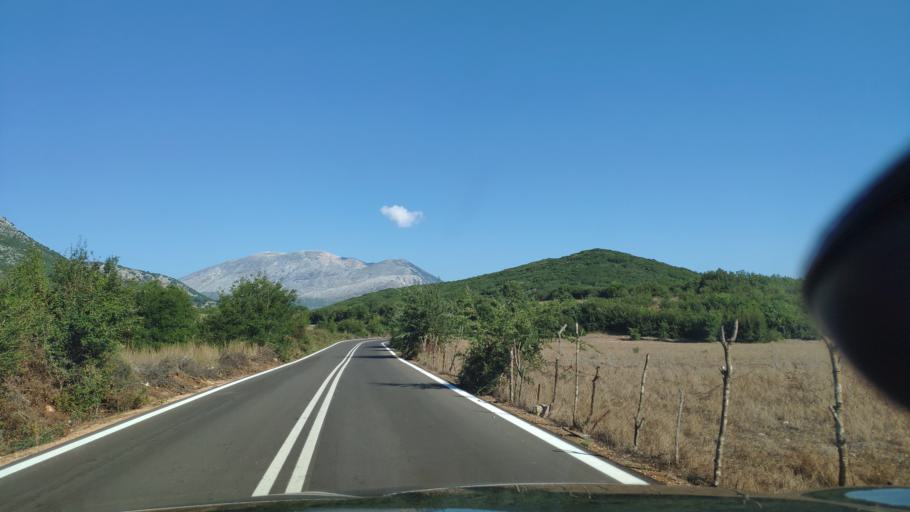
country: GR
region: West Greece
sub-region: Nomos Aitolias kai Akarnanias
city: Fitiai
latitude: 38.6790
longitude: 21.1349
